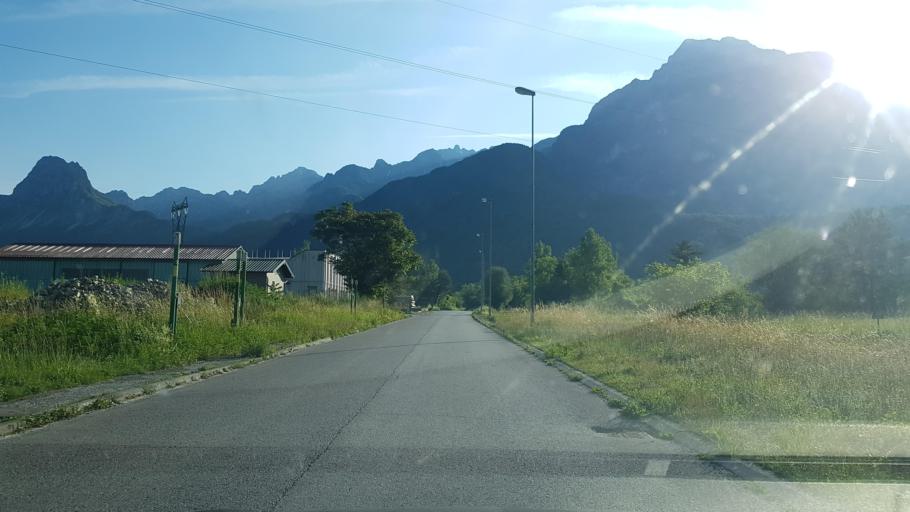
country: IT
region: Friuli Venezia Giulia
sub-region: Provincia di Udine
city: Moggio di Sotto
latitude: 46.4014
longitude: 13.1934
